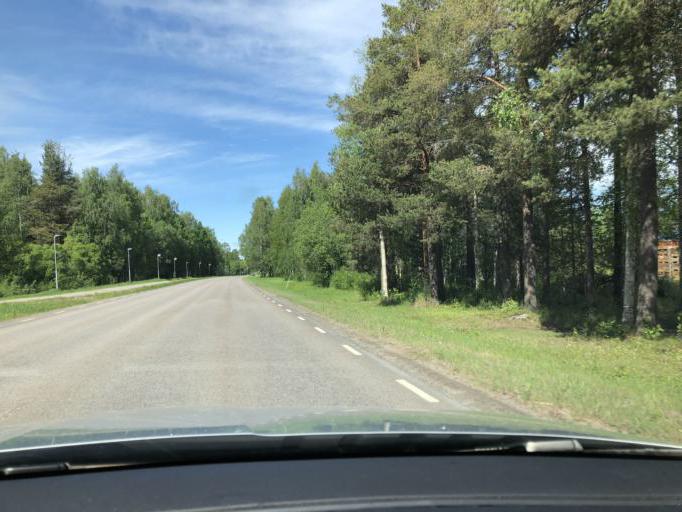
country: SE
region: Norrbotten
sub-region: Pitea Kommun
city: Bergsviken
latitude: 65.3348
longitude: 21.4152
